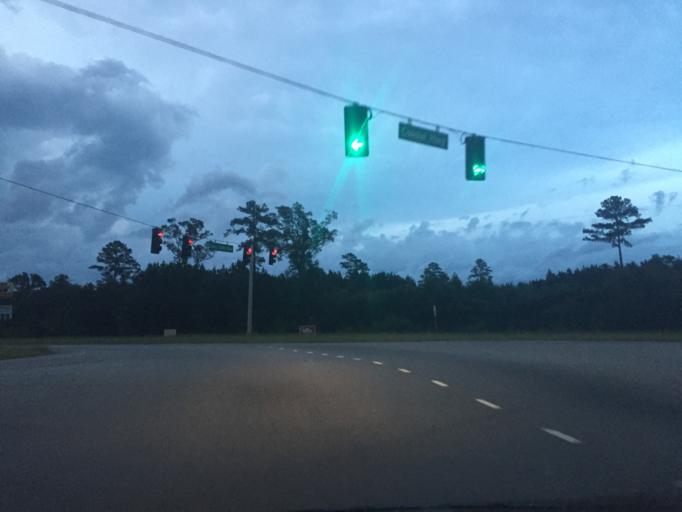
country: US
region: Georgia
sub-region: Liberty County
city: Midway
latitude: 31.8789
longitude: -81.3953
